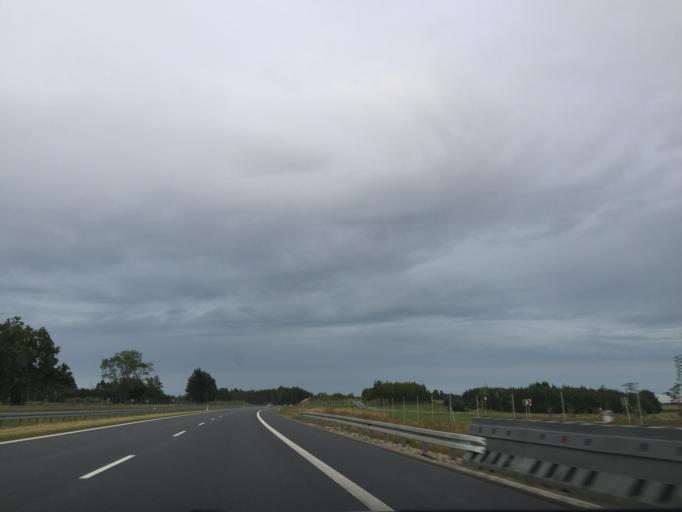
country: PL
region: Podlasie
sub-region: Powiat zambrowski
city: Rutki-Kossaki
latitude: 53.0804
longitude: 22.4457
